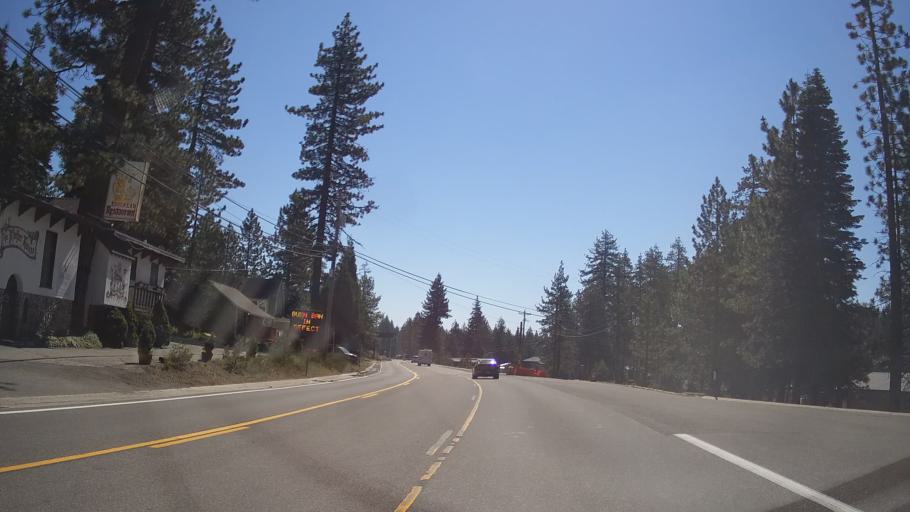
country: US
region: California
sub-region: Placer County
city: Sunnyside-Tahoe City
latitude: 39.1638
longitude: -120.1539
